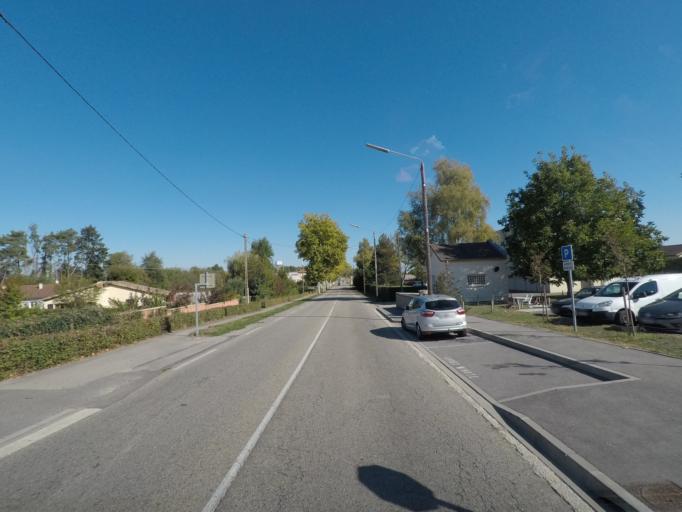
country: FR
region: Rhone-Alpes
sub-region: Departement de l'Ain
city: Servas
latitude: 46.1332
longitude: 5.1654
